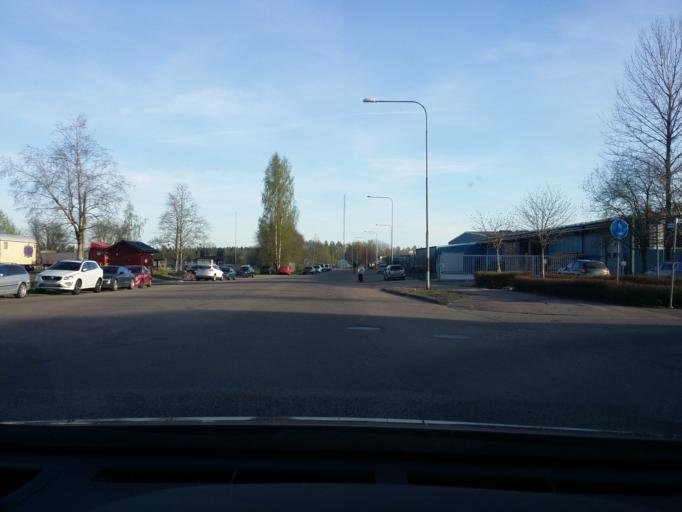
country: SE
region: Dalarna
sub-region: Avesta Kommun
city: Avesta
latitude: 60.1400
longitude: 16.1686
